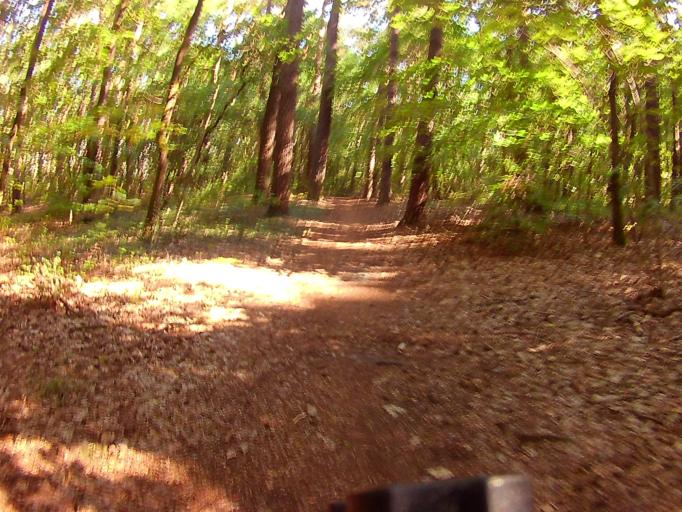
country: DE
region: Berlin
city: Bohnsdorf
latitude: 52.4019
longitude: 13.5869
